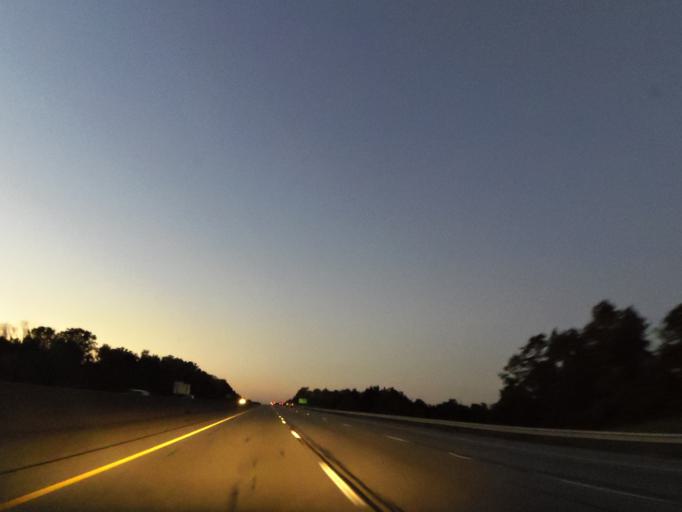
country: US
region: Kentucky
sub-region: Grant County
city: Crittenden
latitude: 38.7981
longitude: -84.6034
